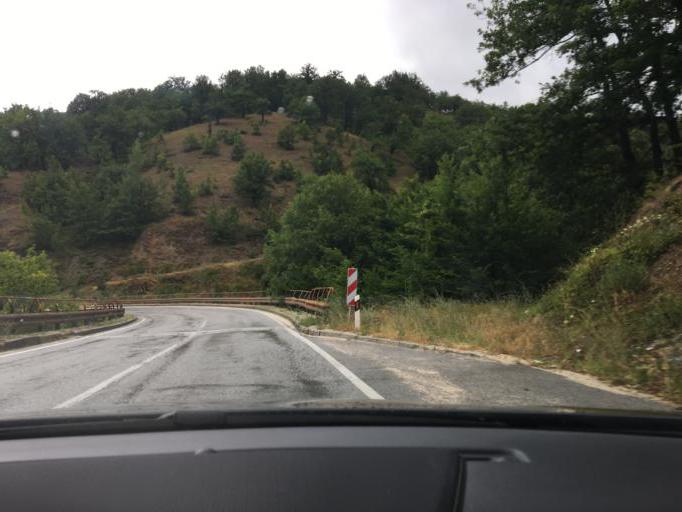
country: MK
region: Kriva Palanka
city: Kriva Palanka
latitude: 42.2202
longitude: 22.4335
